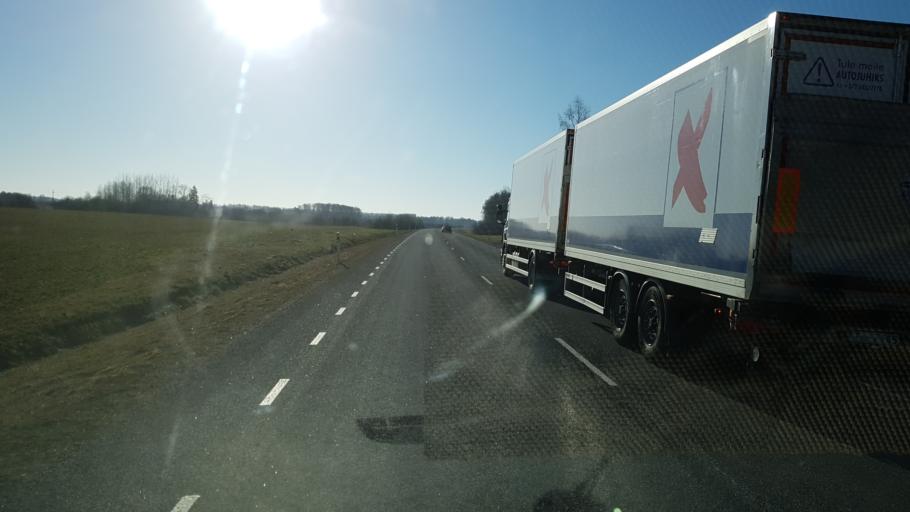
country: EE
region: Jaervamaa
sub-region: Tueri vald
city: Sarevere
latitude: 58.7777
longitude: 25.5004
